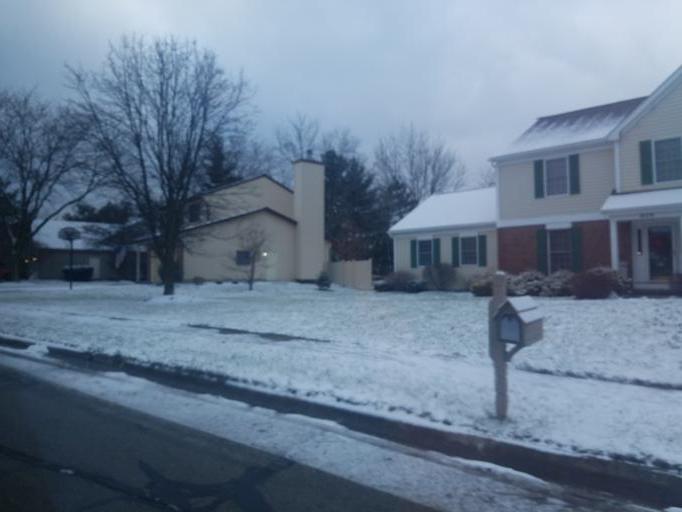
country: US
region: Ohio
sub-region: Franklin County
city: Gahanna
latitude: 40.0394
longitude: -82.8534
